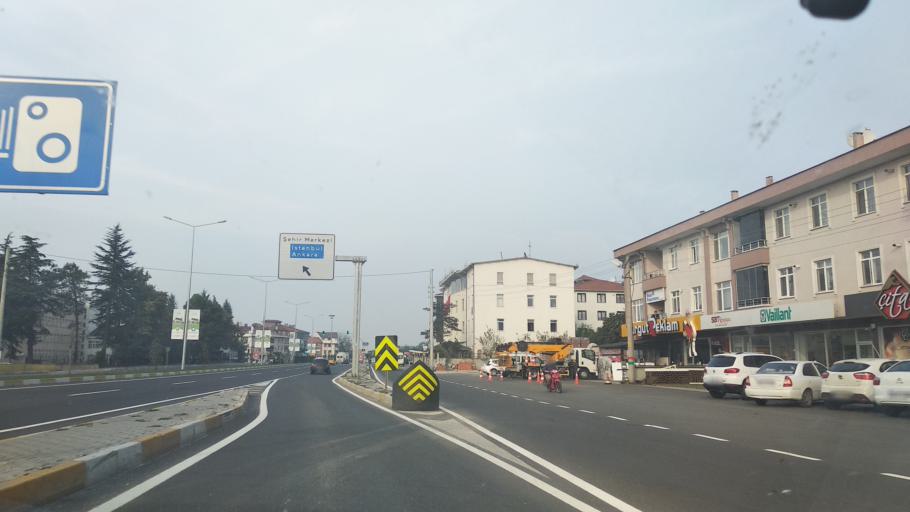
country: TR
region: Duzce
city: Duzce
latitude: 40.8339
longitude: 31.1699
